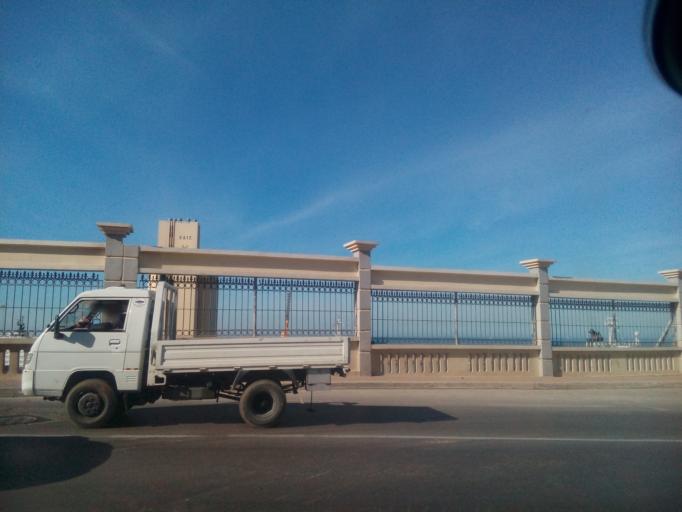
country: DZ
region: Mostaganem
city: Mostaganem
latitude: 35.9337
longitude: 0.0792
